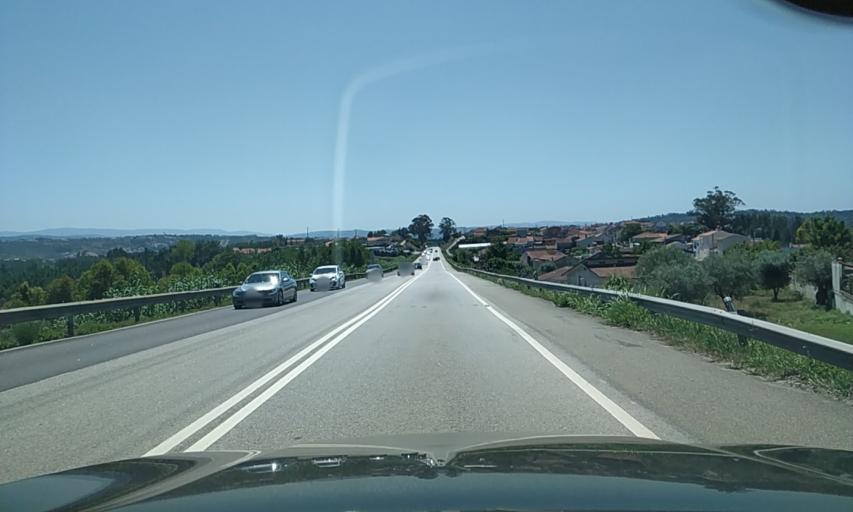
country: PT
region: Aveiro
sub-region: Mealhada
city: Pampilhosa do Botao
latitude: 40.2965
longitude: -8.4461
